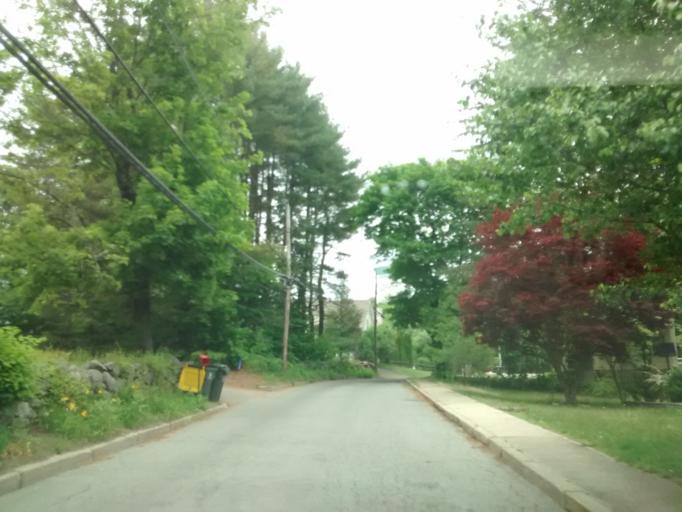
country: US
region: Rhode Island
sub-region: Providence County
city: Harrisville
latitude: 41.9683
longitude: -71.6728
